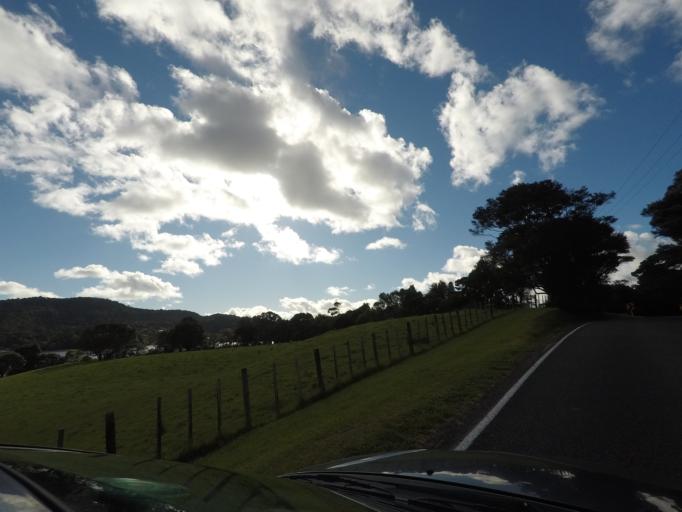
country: NZ
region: Auckland
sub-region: Auckland
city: Titirangi
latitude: -37.0057
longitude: 174.5627
